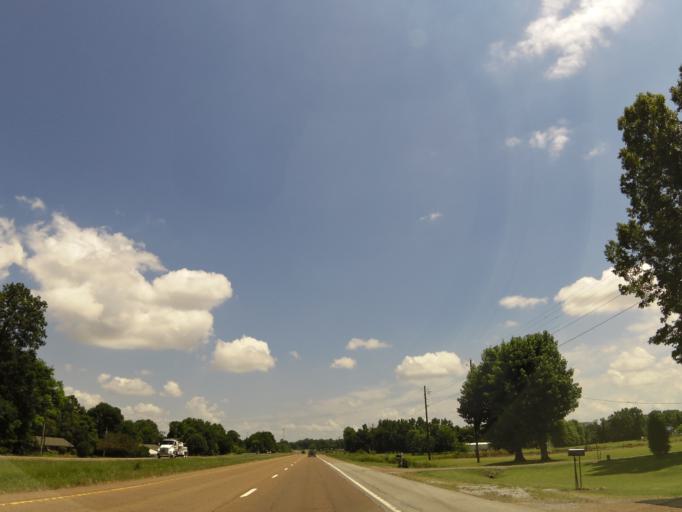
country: US
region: Tennessee
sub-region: Lauderdale County
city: Halls
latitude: 35.9251
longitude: -89.2811
